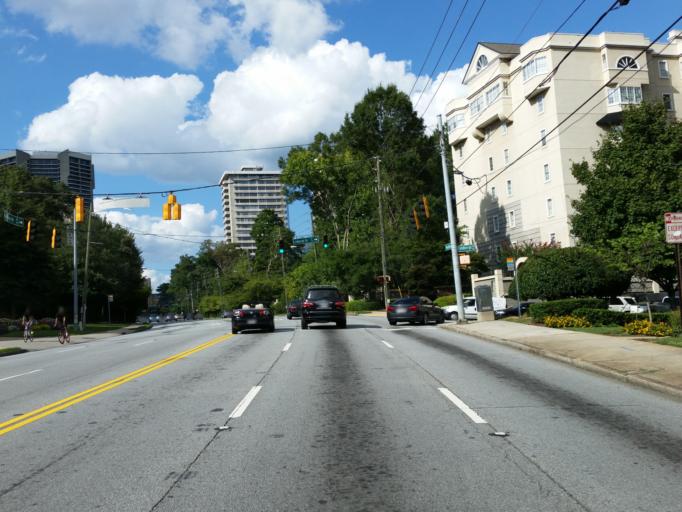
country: US
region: Georgia
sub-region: DeKalb County
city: North Atlanta
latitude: 33.8225
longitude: -84.3876
